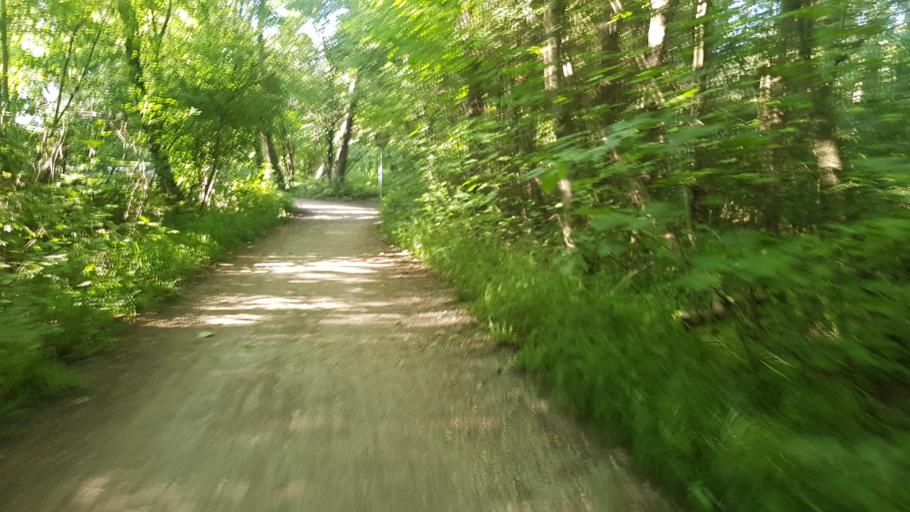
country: DE
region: Bavaria
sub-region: Upper Bavaria
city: Karlsfeld
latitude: 48.2440
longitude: 11.4907
